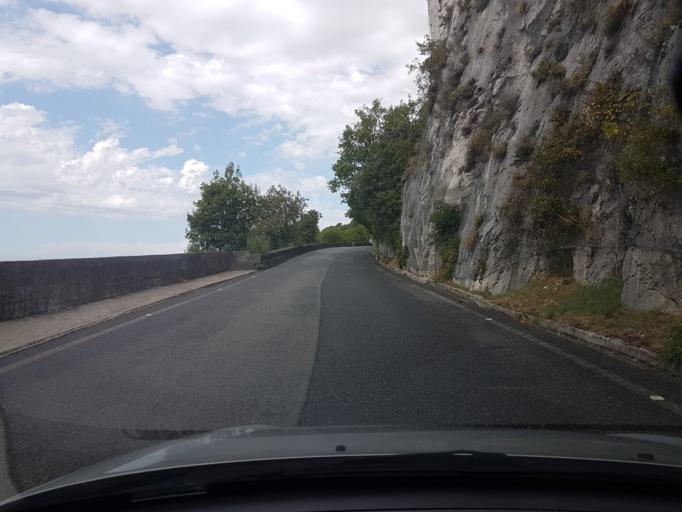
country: IT
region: Friuli Venezia Giulia
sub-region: Provincia di Trieste
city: Prosecco-Contovello
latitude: 45.6967
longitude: 13.7411
